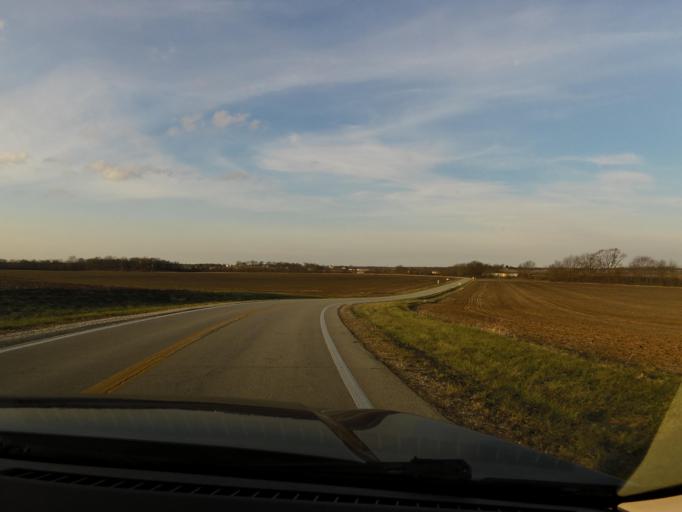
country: US
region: Illinois
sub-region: Fayette County
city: Vandalia
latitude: 38.9488
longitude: -89.1473
